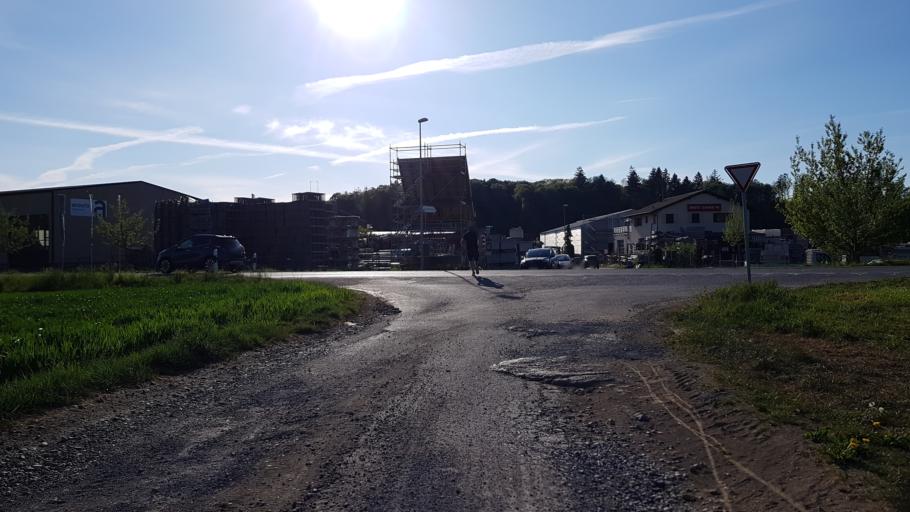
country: CH
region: Aargau
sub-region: Bezirk Bremgarten
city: Sarmenstorf
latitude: 47.3000
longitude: 8.2465
